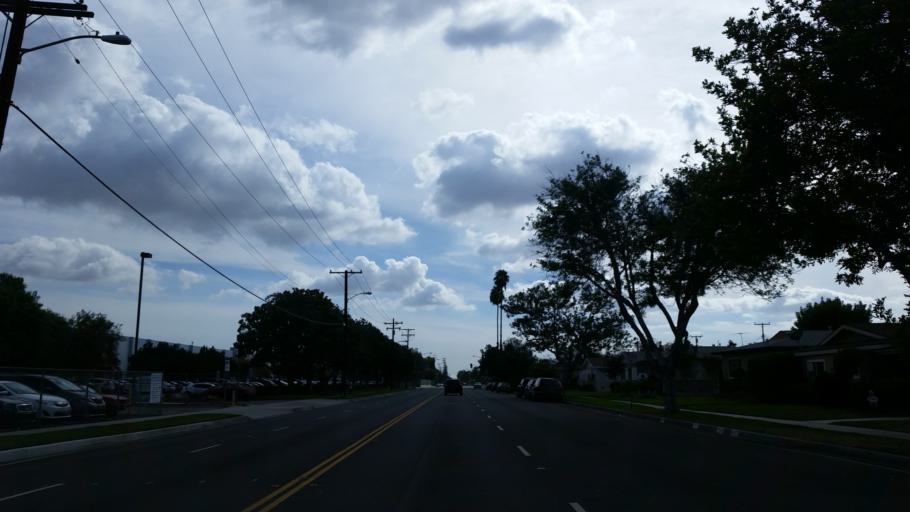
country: US
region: California
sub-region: Los Angeles County
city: Downey
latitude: 33.9158
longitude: -118.1342
